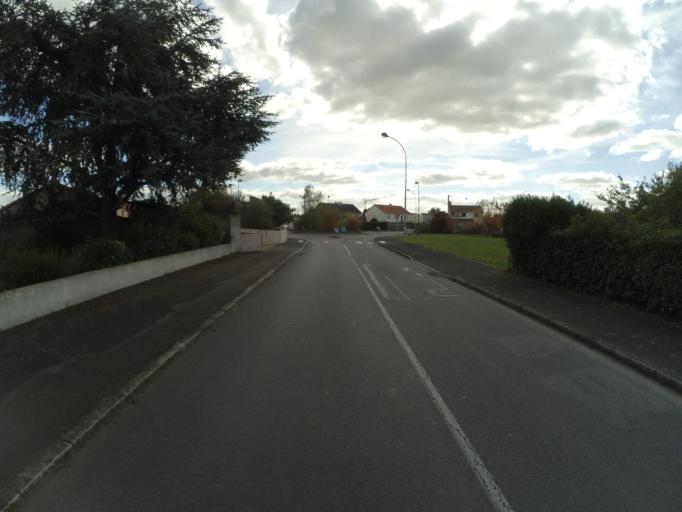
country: FR
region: Pays de la Loire
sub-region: Departement de la Loire-Atlantique
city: La Chapelle-Heulin
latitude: 47.1805
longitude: -1.3406
